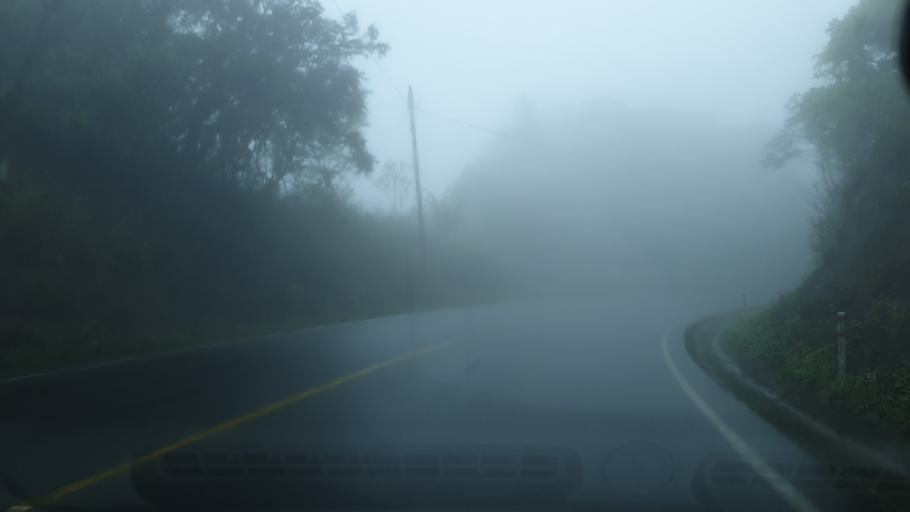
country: EC
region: Manabi
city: Jipijapa
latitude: -1.3467
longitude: -80.6552
